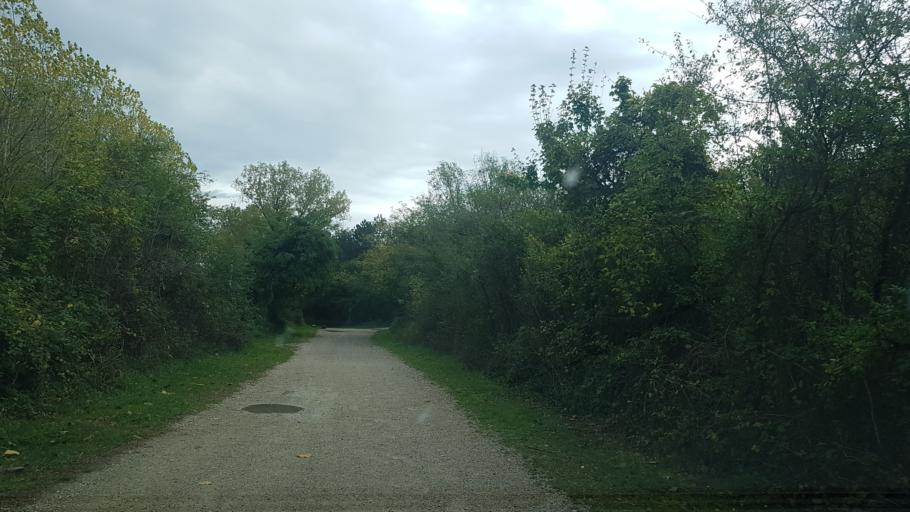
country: IT
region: Friuli Venezia Giulia
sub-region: Provincia di Gorizia
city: Ronchi dei Legionari
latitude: 45.8192
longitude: 13.5244
